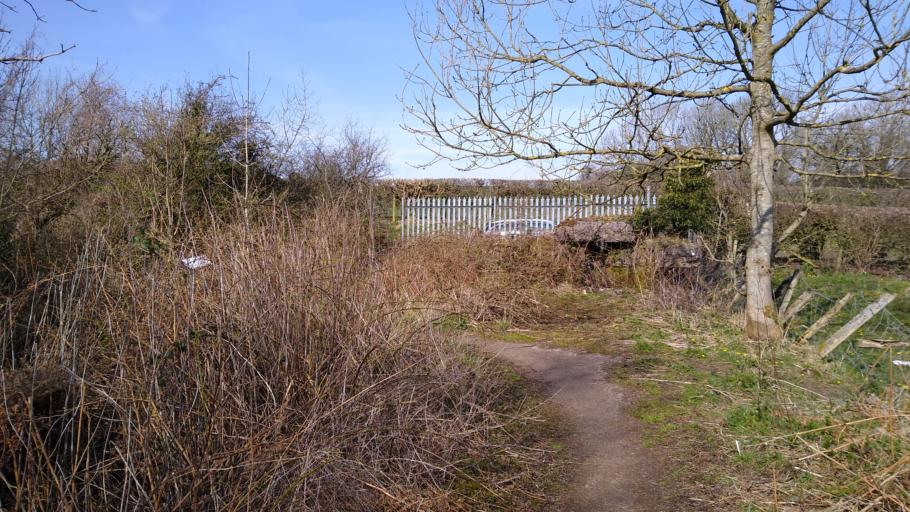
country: GB
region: England
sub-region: Cumbria
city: Dearham
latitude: 54.6744
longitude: -3.4148
